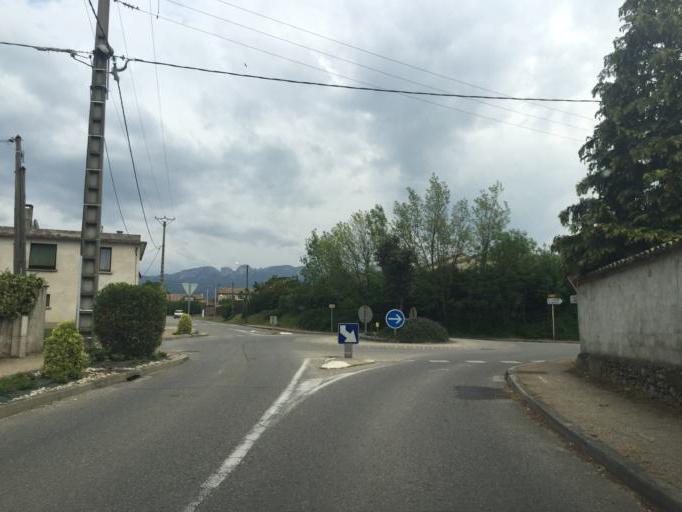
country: FR
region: Rhone-Alpes
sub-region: Departement de la Drome
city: Chatuzange-le-Goubet
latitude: 44.9644
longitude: 5.0798
